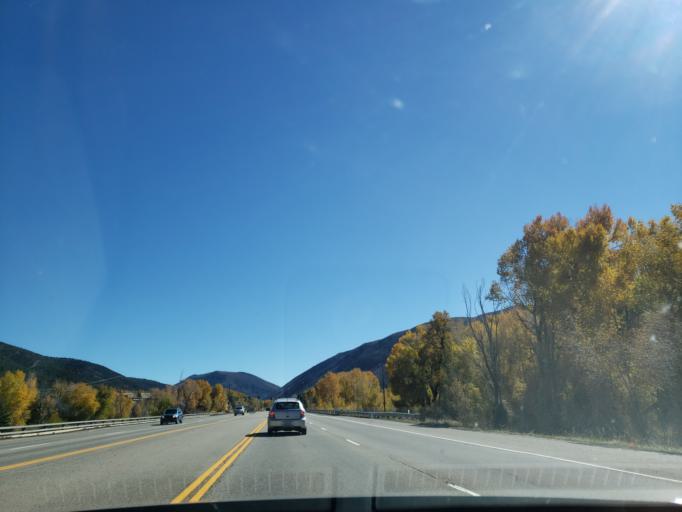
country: US
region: Colorado
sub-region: Eagle County
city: Basalt
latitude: 39.3605
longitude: -107.0288
